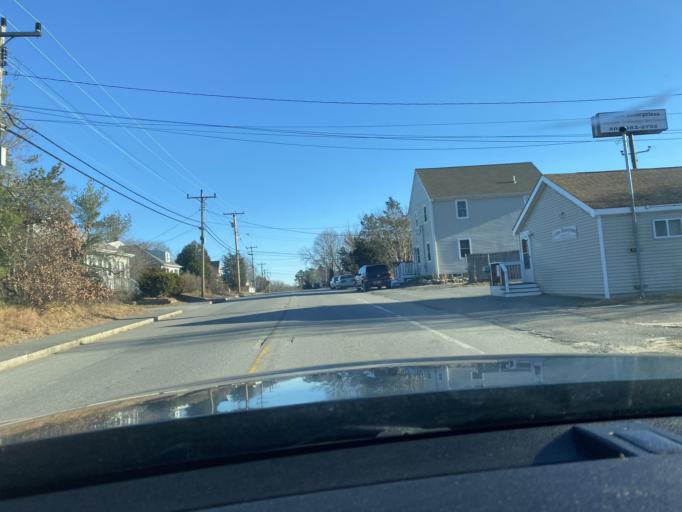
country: US
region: Massachusetts
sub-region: Plymouth County
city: Onset
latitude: 41.7669
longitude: -70.6859
